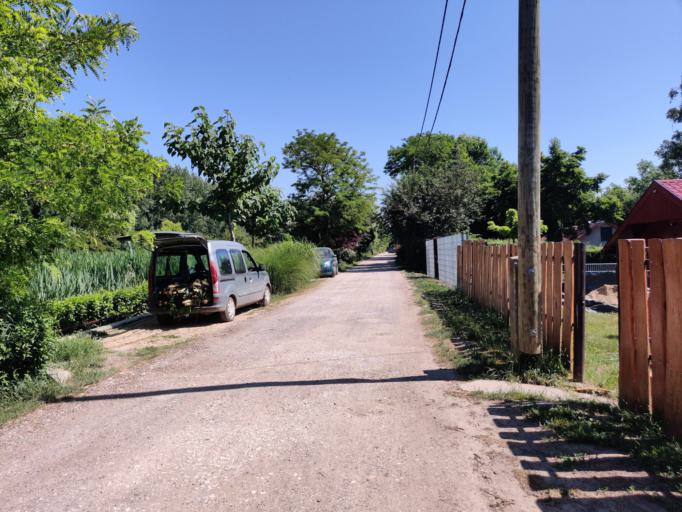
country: HU
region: Hajdu-Bihar
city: Balmazujvaros
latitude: 47.5995
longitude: 21.3763
